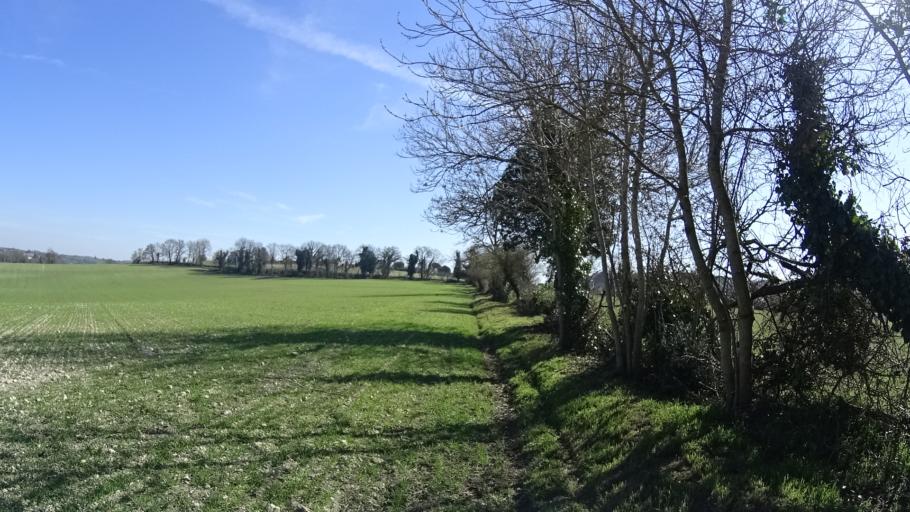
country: FR
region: Aquitaine
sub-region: Departement de la Dordogne
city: Riberac
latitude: 45.2262
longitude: 0.3395
